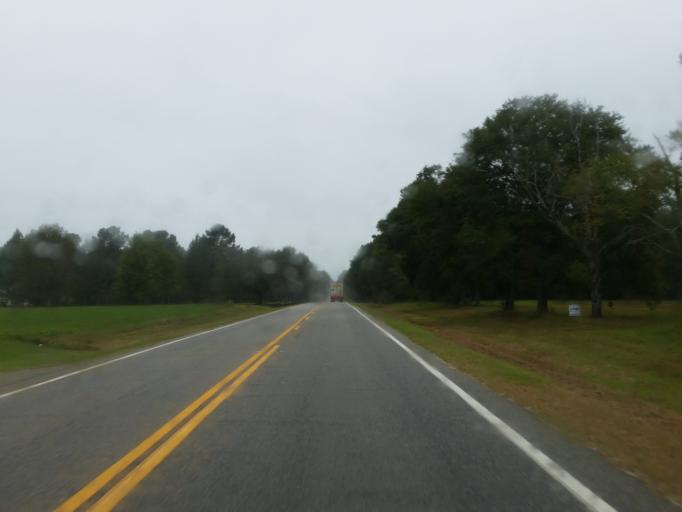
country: US
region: Georgia
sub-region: Berrien County
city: Ray City
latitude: 31.1023
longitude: -83.2761
